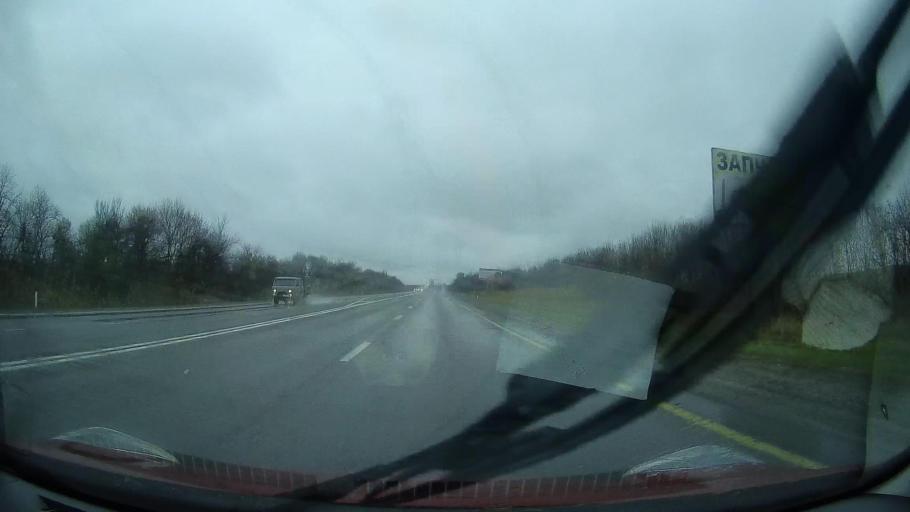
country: RU
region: Stavropol'skiy
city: Nevinnomyssk
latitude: 44.6345
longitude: 42.0052
